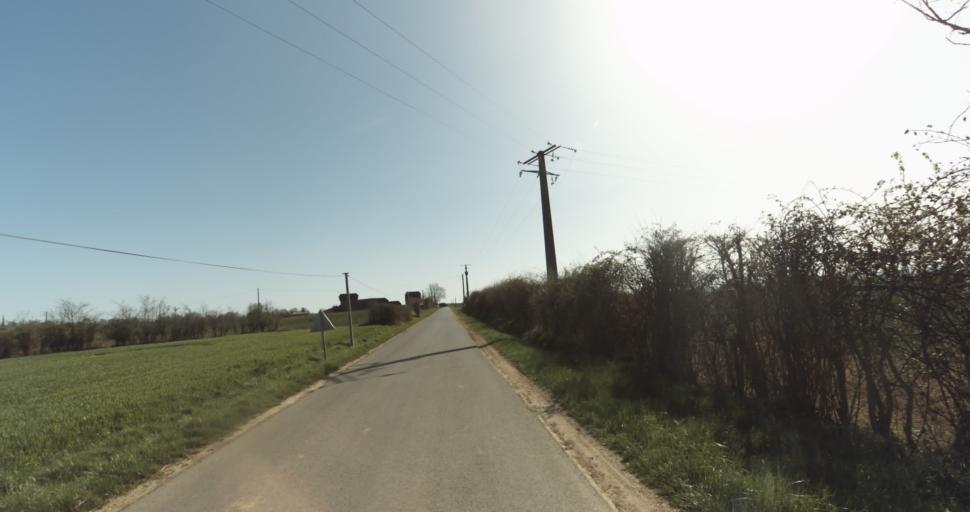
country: FR
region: Lower Normandy
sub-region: Departement de l'Orne
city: Trun
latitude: 48.9050
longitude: 0.0337
